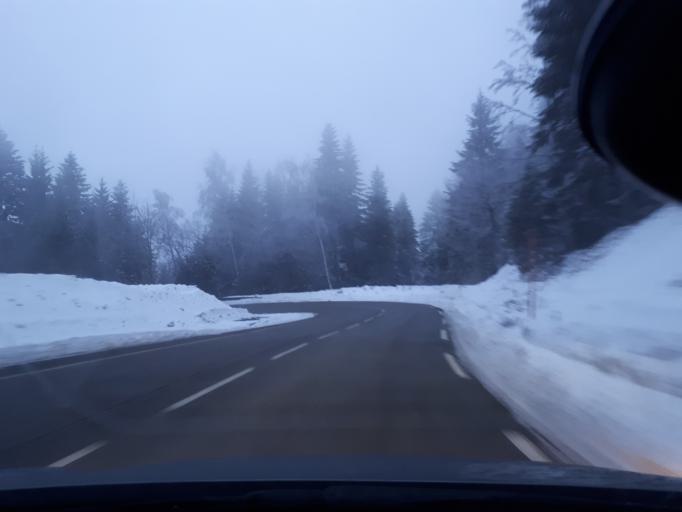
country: FR
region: Rhone-Alpes
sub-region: Departement de l'Isere
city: Vaulnaveys-le-Bas
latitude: 45.0928
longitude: 5.8521
